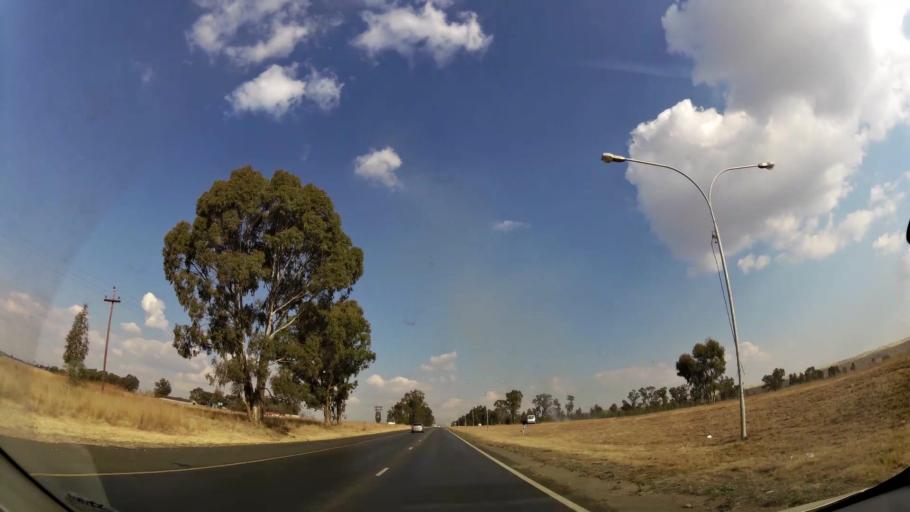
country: ZA
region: Gauteng
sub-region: Ekurhuleni Metropolitan Municipality
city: Brakpan
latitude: -26.3259
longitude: 28.3390
